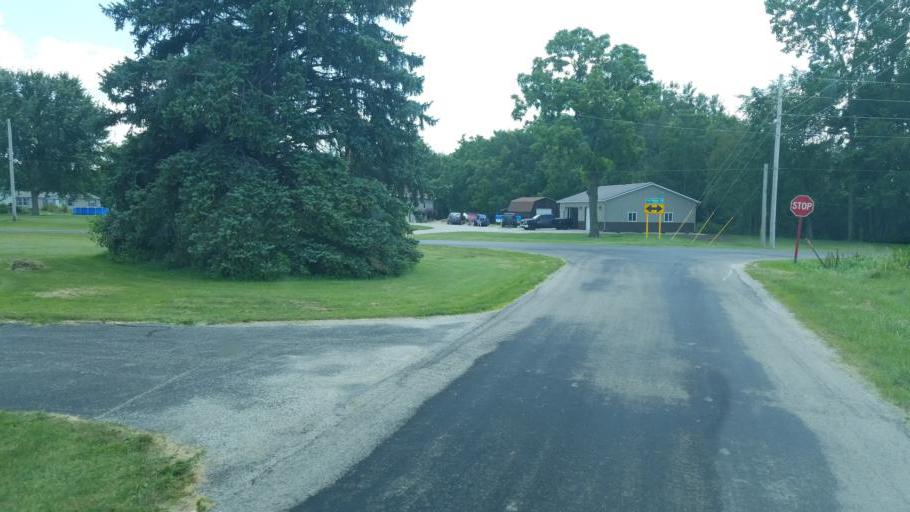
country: US
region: Ohio
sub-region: Marion County
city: Marion
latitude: 40.6524
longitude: -83.0923
